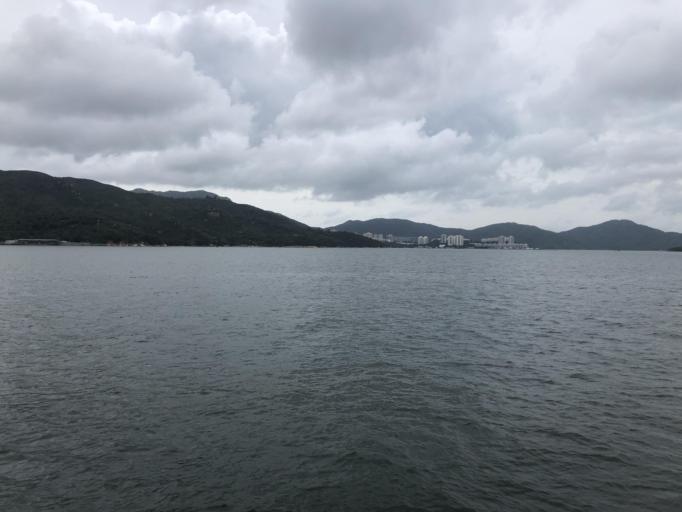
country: HK
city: Yung Shue Wan
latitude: 22.2672
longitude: 114.0308
